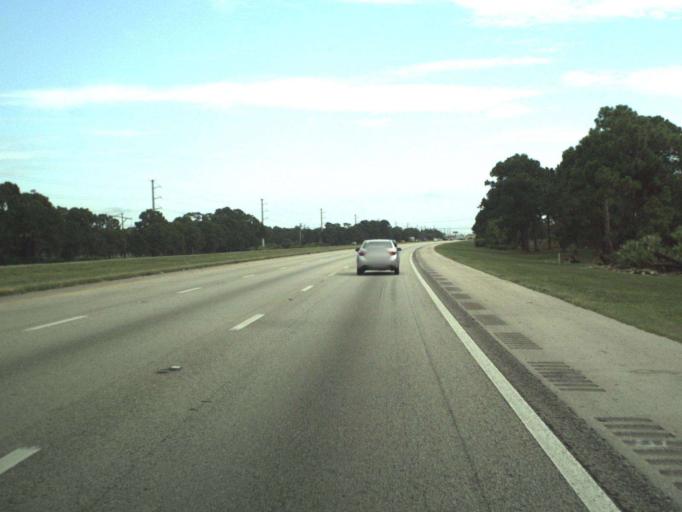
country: US
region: Florida
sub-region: Saint Lucie County
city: River Park
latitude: 27.3331
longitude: -80.4138
